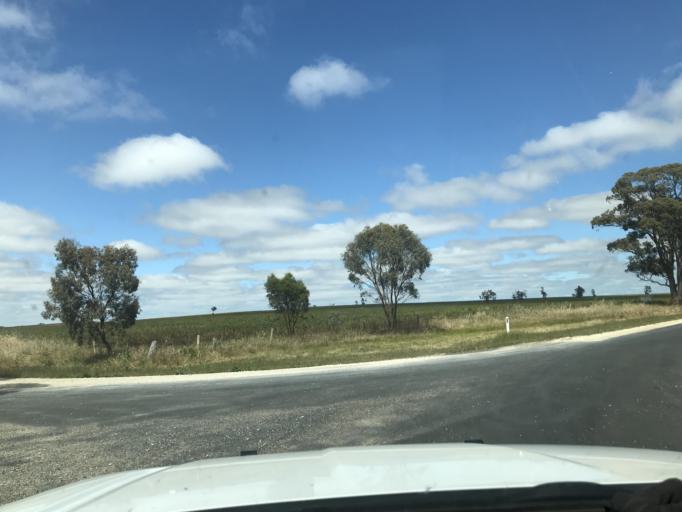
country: AU
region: South Australia
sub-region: Tatiara
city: Bordertown
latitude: -36.3059
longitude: 141.0923
